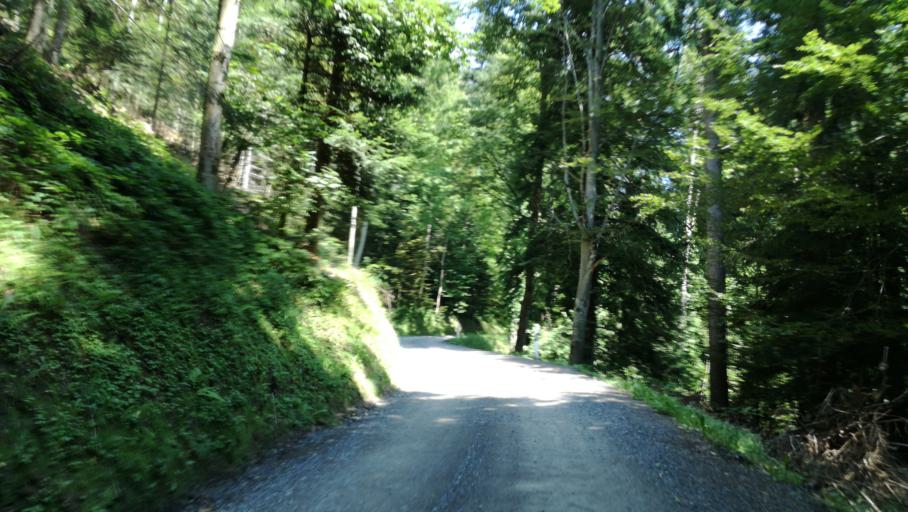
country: CH
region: Zug
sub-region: Zug
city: Unterageri
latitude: 47.1429
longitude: 8.5962
